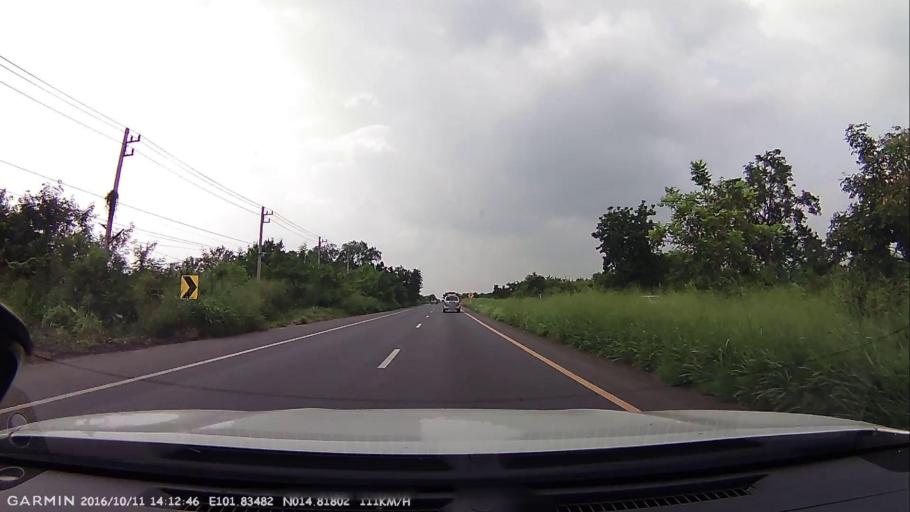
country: TH
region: Nakhon Ratchasima
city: Sung Noen
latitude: 14.8180
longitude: 101.8348
